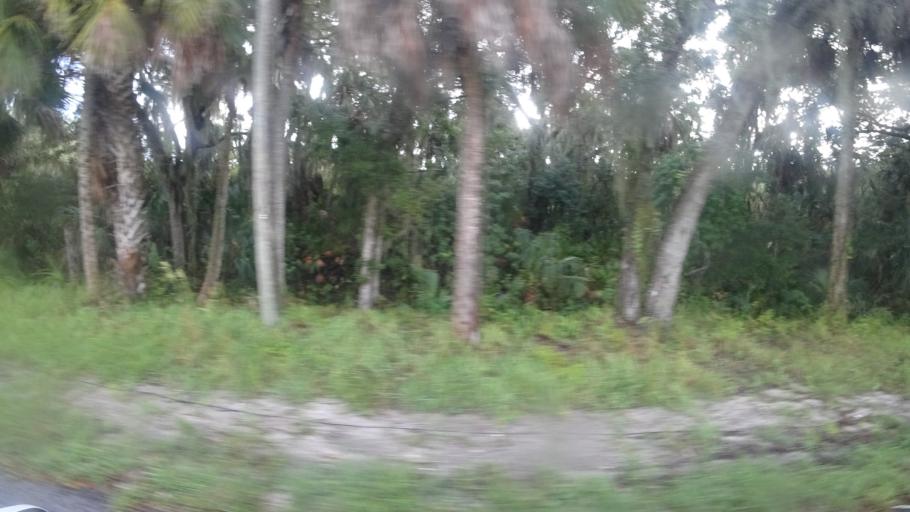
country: US
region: Florida
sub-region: Manatee County
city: Ellenton
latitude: 27.5336
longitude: -82.4827
